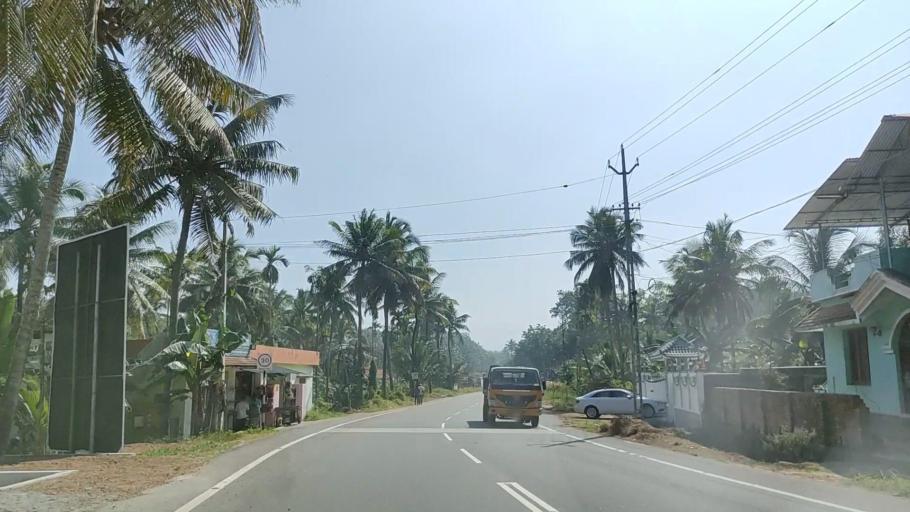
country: IN
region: Kerala
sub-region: Kollam
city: Punalur
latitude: 8.9186
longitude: 77.0391
